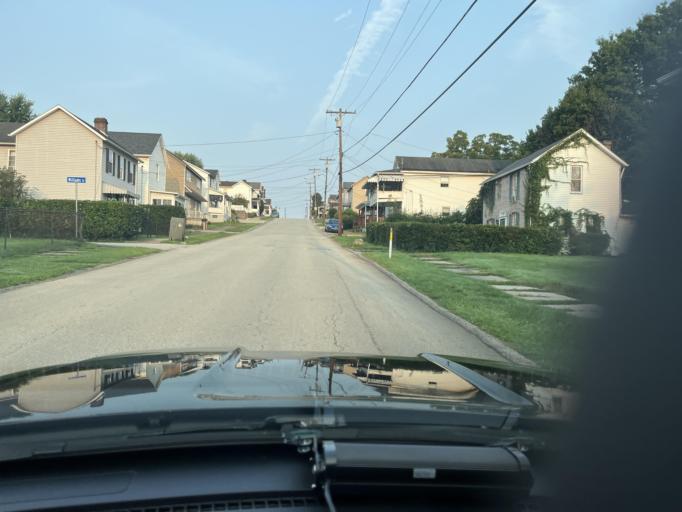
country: US
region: Pennsylvania
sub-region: Fayette County
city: Uniontown
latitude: 39.8911
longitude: -79.7267
